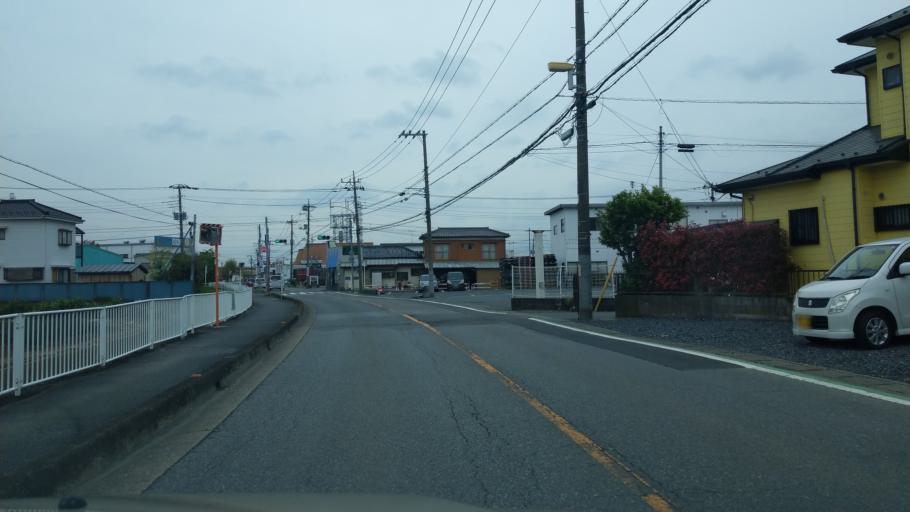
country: JP
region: Saitama
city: Kasukabe
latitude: 35.9475
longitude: 139.7269
